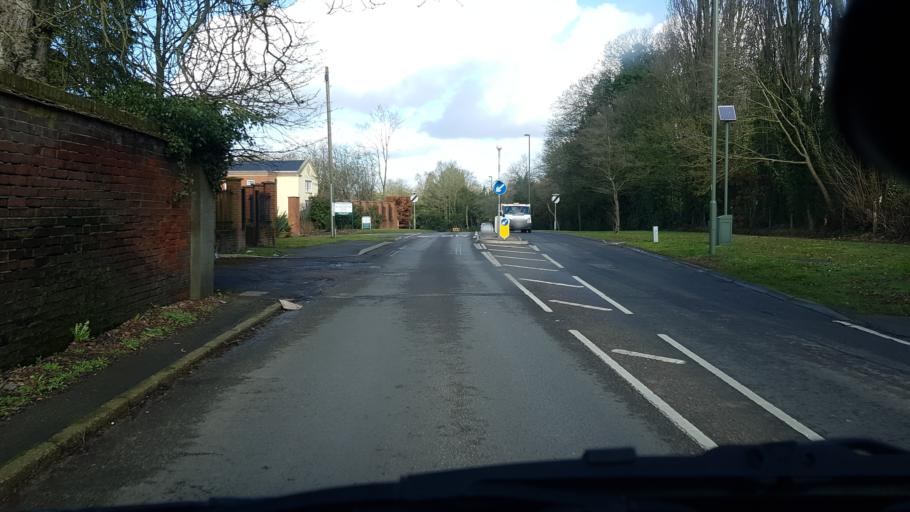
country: GB
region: England
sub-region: Surrey
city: Guildford
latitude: 51.2651
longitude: -0.5979
